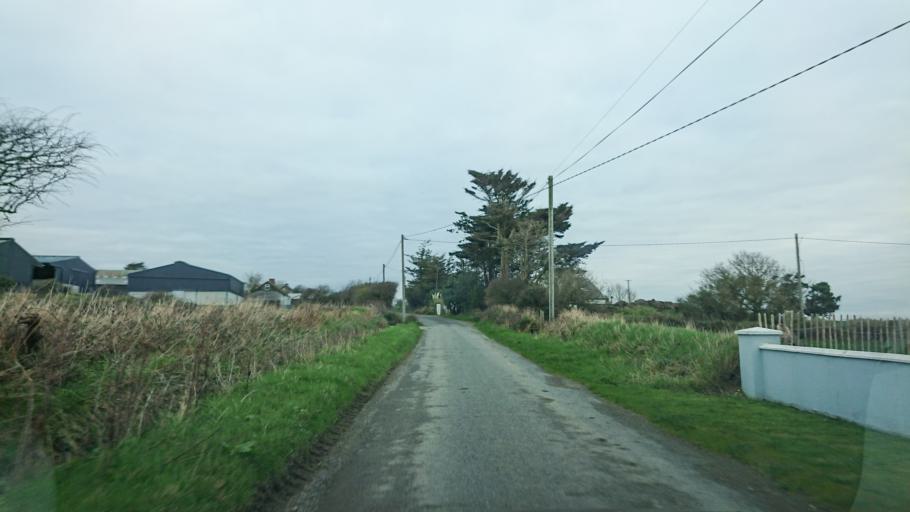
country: IE
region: Munster
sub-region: Waterford
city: Tra Mhor
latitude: 52.1407
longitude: -7.1820
